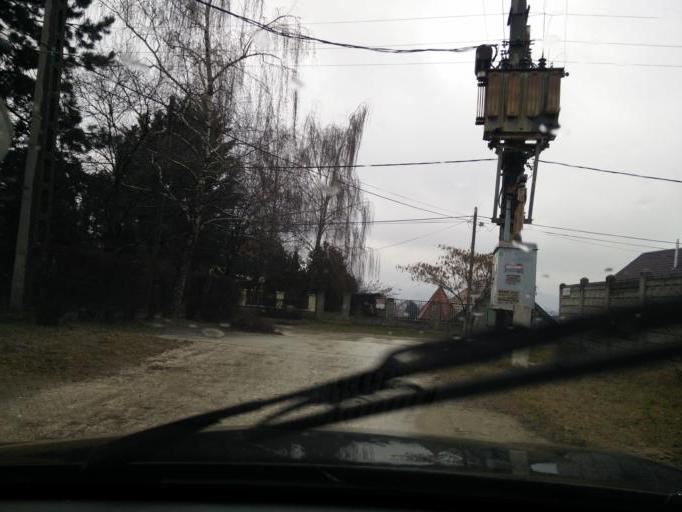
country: HU
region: Pest
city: Pilisszentivan
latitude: 47.6144
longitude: 18.8936
